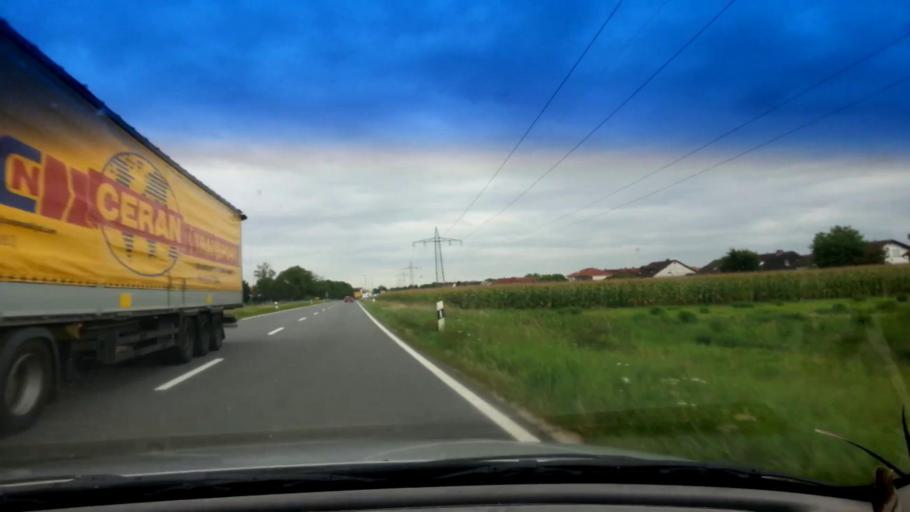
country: DE
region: Bavaria
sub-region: Upper Franconia
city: Hirschaid
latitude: 49.8259
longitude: 10.9945
